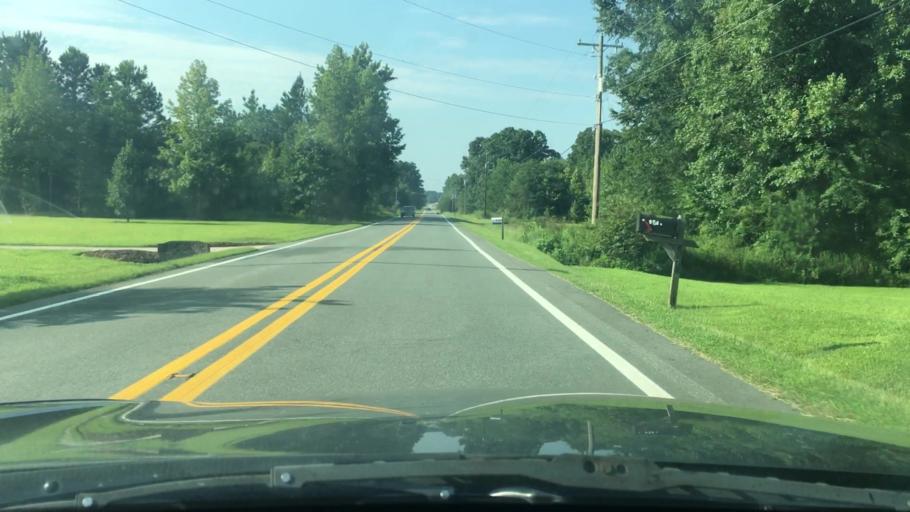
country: US
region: North Carolina
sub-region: Alamance County
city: Green Level
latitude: 36.2122
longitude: -79.3217
